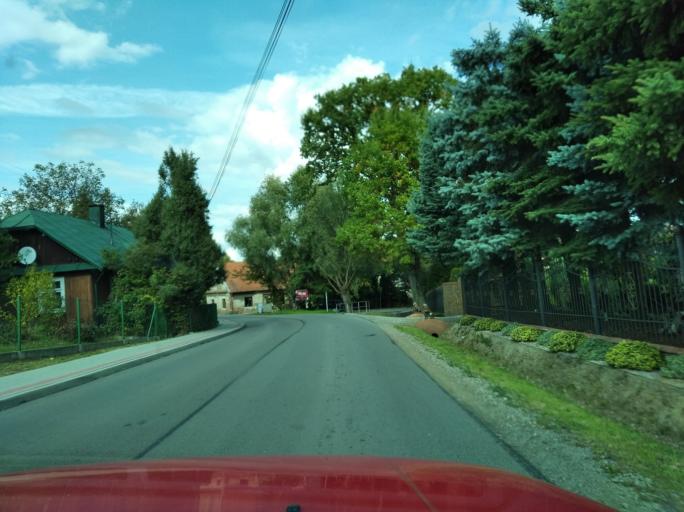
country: PL
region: Subcarpathian Voivodeship
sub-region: Powiat rzeszowski
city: Tyczyn
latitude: 49.9578
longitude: 22.0325
